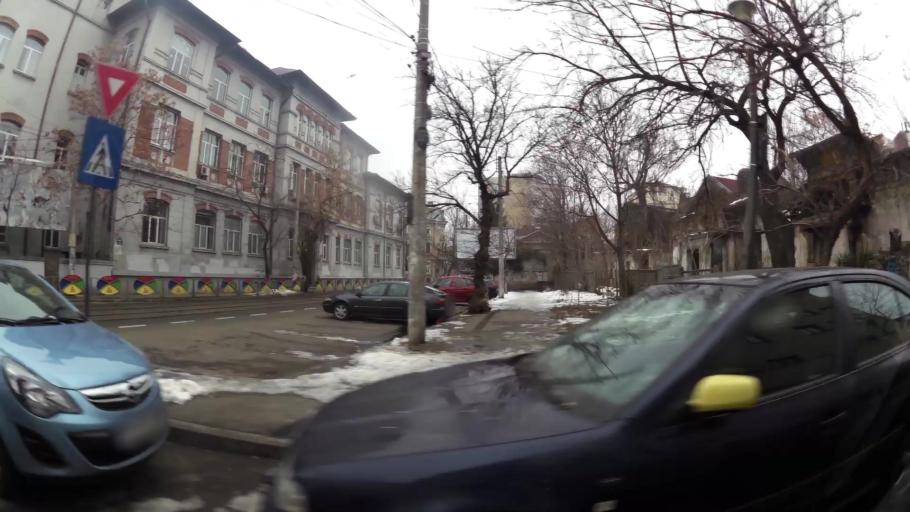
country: RO
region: Bucuresti
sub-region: Municipiul Bucuresti
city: Bucharest
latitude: 44.4378
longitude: 26.1209
